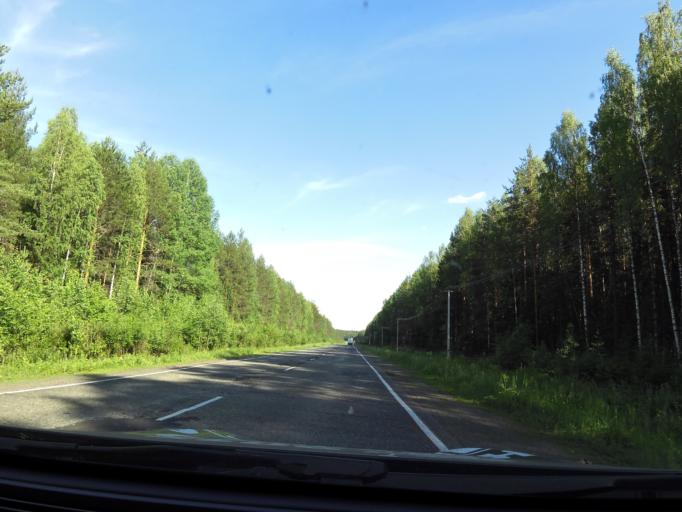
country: RU
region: Kirov
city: Dubrovka
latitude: 58.9106
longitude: 51.1737
